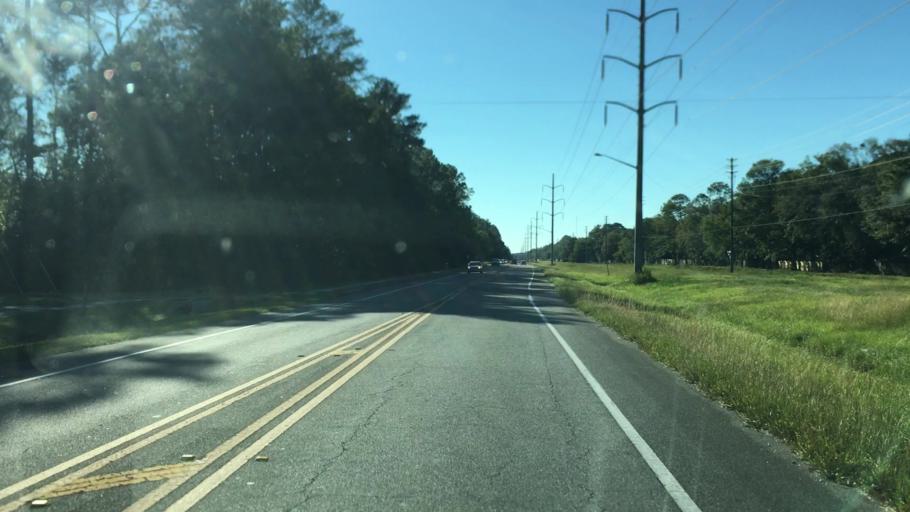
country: US
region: Florida
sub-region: Alachua County
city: Gainesville
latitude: 29.7033
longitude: -82.3555
